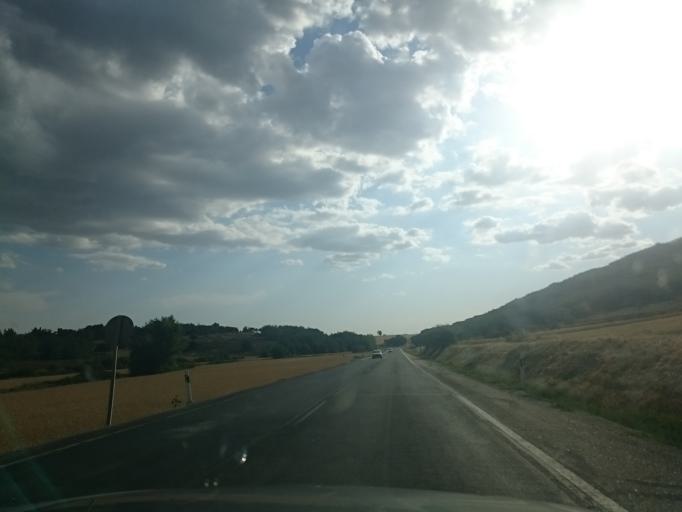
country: ES
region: Castille and Leon
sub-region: Provincia de Burgos
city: Ibeas de Juarros
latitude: 42.3414
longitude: -3.5012
